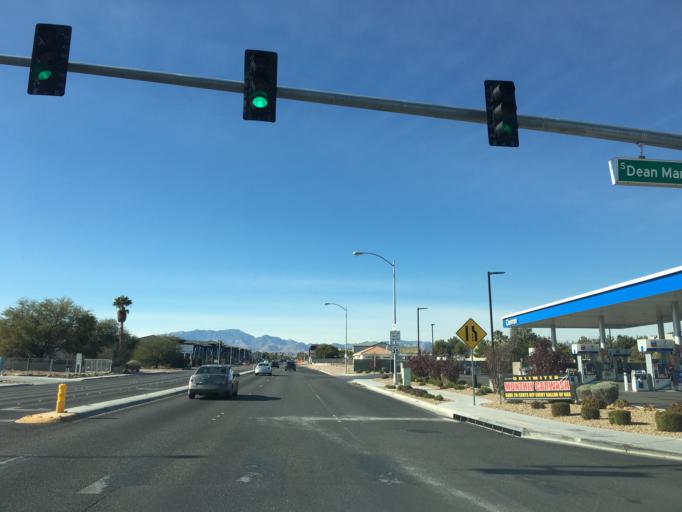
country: US
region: Nevada
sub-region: Clark County
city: Enterprise
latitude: 35.9991
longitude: -115.1837
